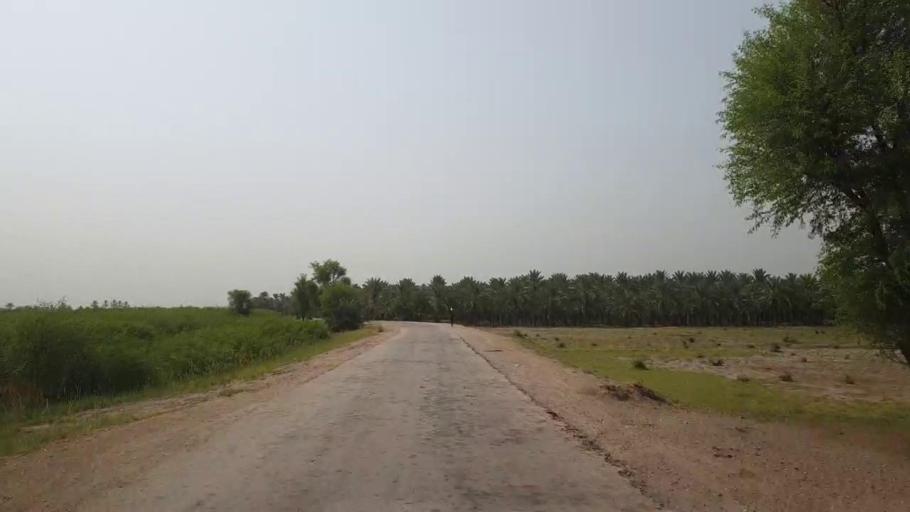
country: PK
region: Sindh
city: Gambat
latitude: 27.4305
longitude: 68.5346
